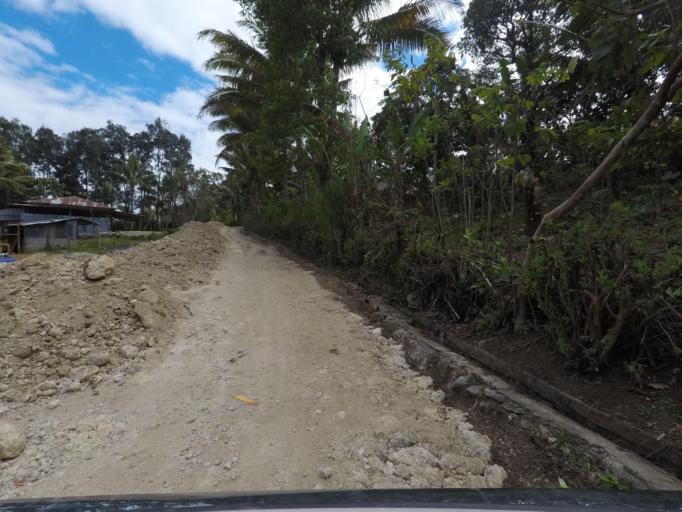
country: TL
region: Baucau
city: Venilale
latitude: -8.6429
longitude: 126.3907
